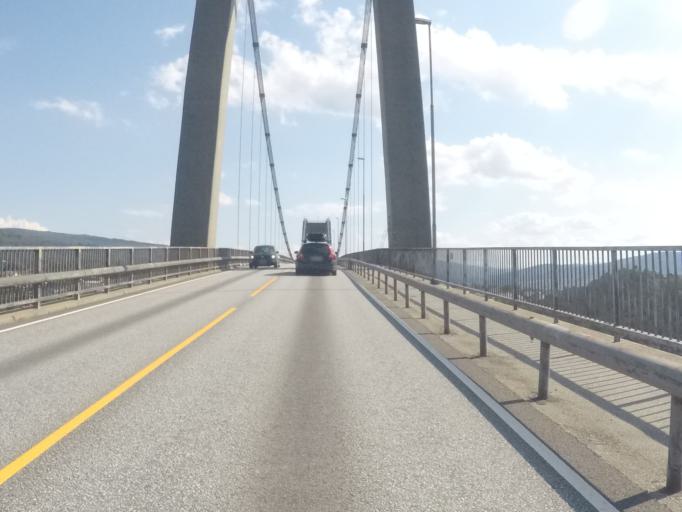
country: NO
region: Hordaland
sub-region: Lindas
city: Knarvik
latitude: 60.5427
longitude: 5.2704
